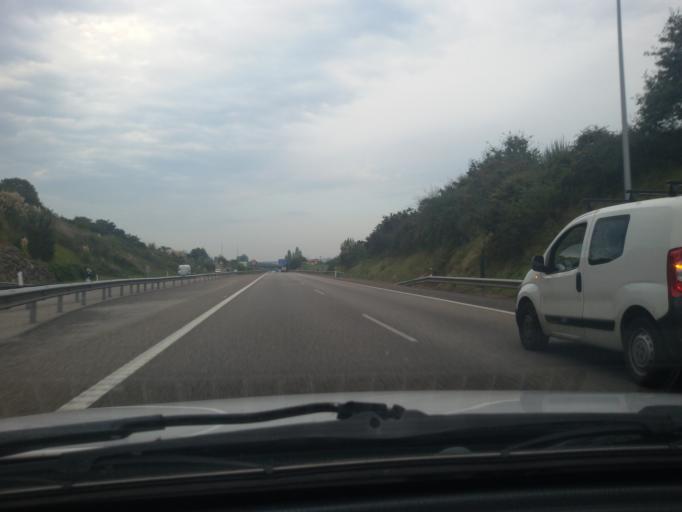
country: ES
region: Asturias
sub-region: Province of Asturias
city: Lugones
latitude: 43.3891
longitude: -5.8276
